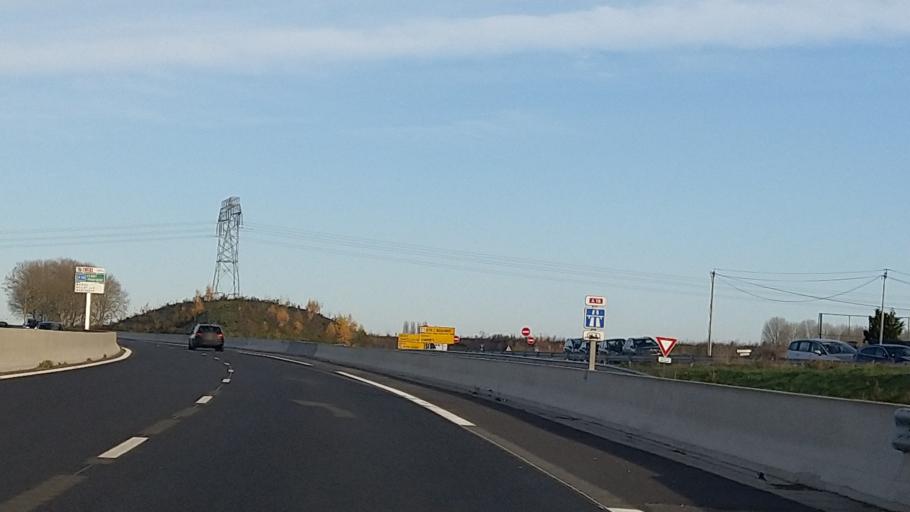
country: FR
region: Ile-de-France
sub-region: Departement du Val-d'Oise
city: Moisselles
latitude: 49.0575
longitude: 2.3319
